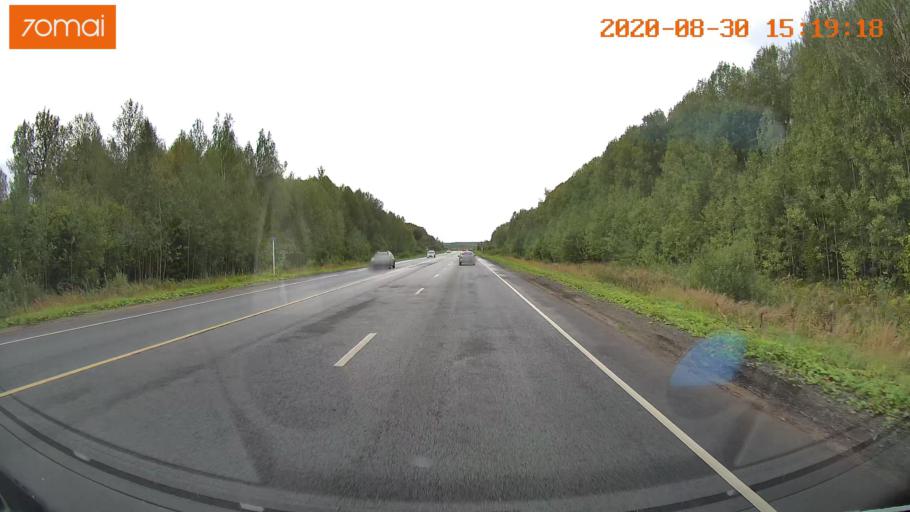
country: RU
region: Ivanovo
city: Rodniki
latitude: 57.1131
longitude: 41.7842
